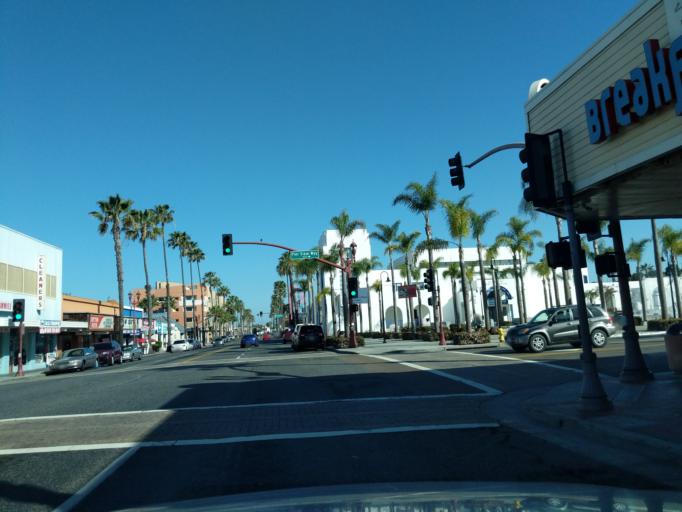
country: US
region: California
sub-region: San Diego County
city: Oceanside
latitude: 33.1966
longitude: -117.3801
